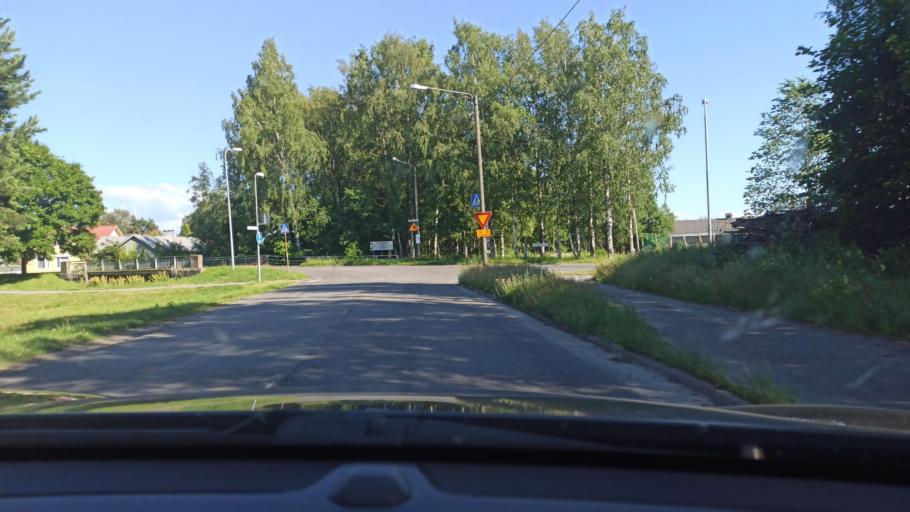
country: FI
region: Satakunta
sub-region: Pori
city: Pori
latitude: 61.4952
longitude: 21.8147
